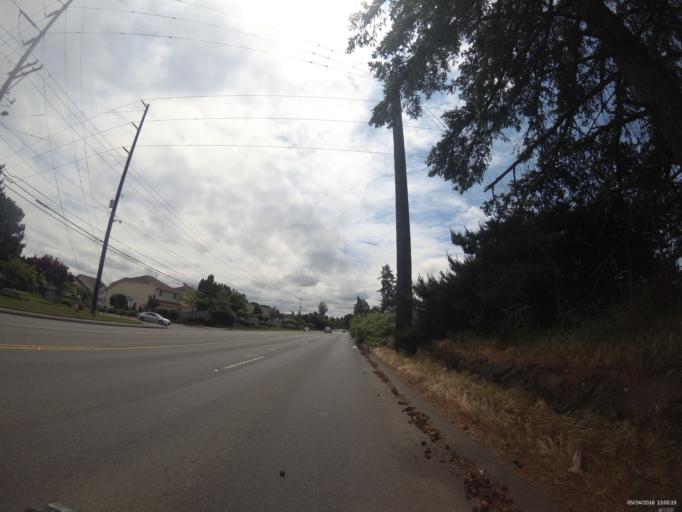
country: US
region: Washington
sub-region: Pierce County
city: Lakewood
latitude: 47.1864
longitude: -122.5087
